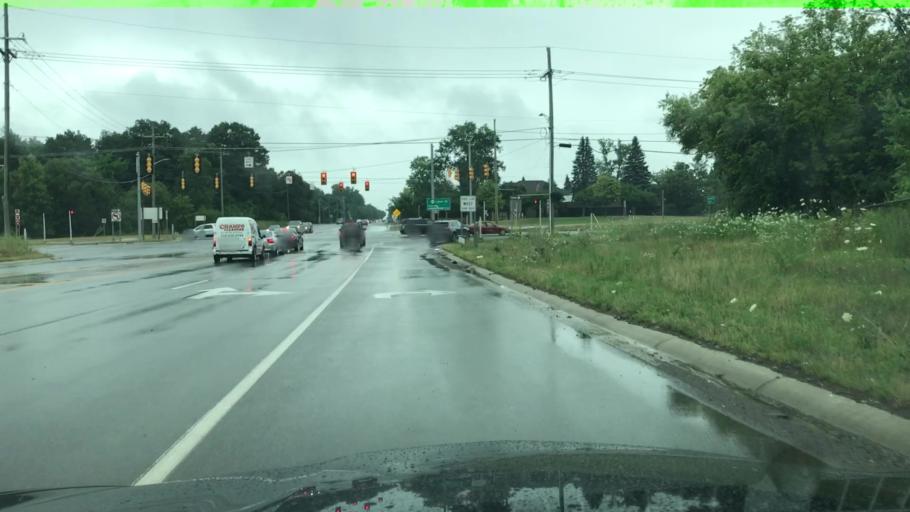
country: US
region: Michigan
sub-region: Oakland County
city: Auburn Hills
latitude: 42.7229
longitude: -83.2439
